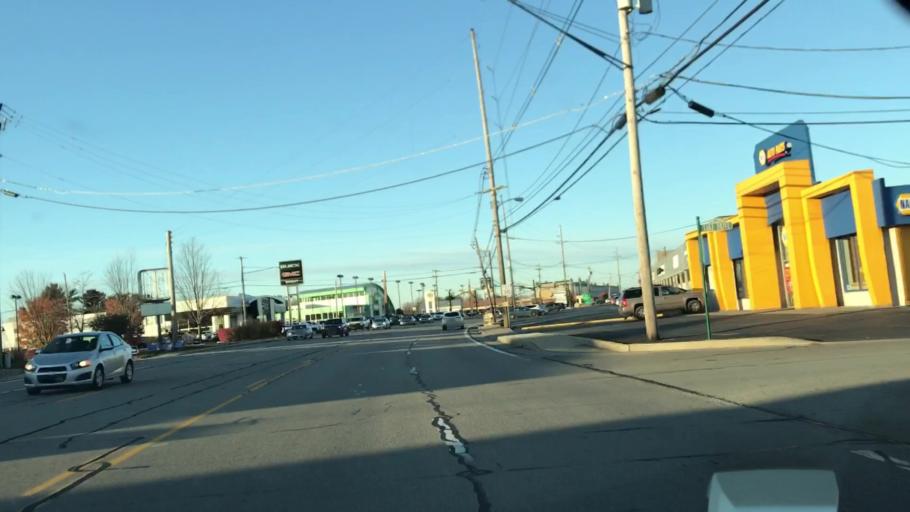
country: US
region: Pennsylvania
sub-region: Allegheny County
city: Bradford Woods
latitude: 40.6171
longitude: -80.0555
